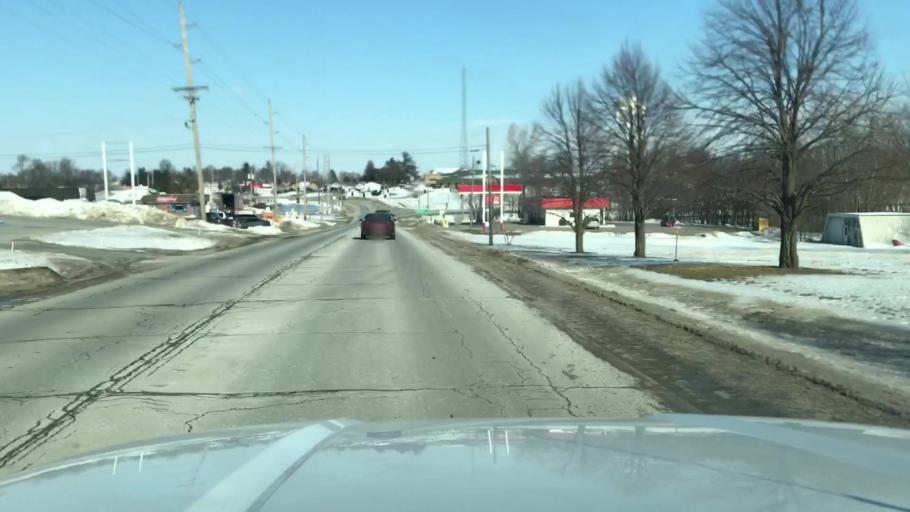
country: US
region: Missouri
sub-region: Andrew County
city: Savannah
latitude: 39.9426
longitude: -94.8219
